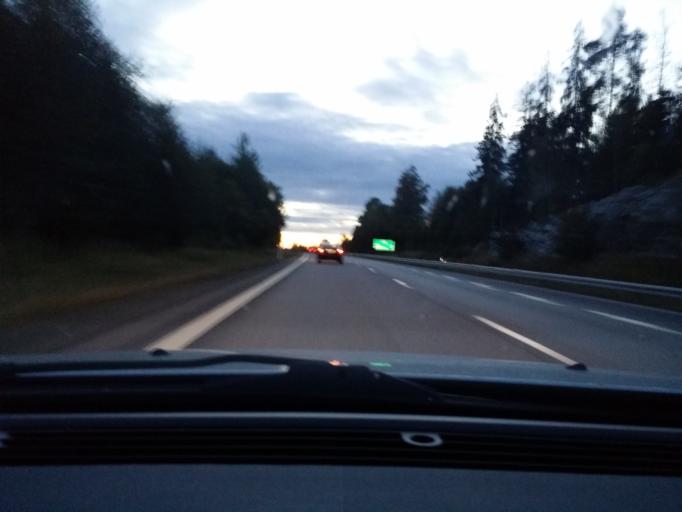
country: SE
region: Uppsala
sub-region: Enkopings Kommun
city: Grillby
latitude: 59.6378
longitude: 17.2672
